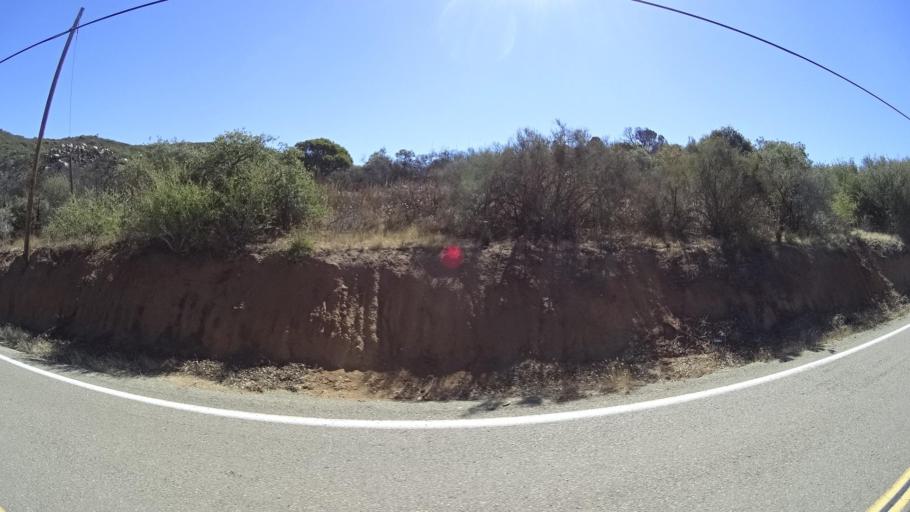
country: US
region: California
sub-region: San Diego County
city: Descanso
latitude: 32.7815
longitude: -116.6654
